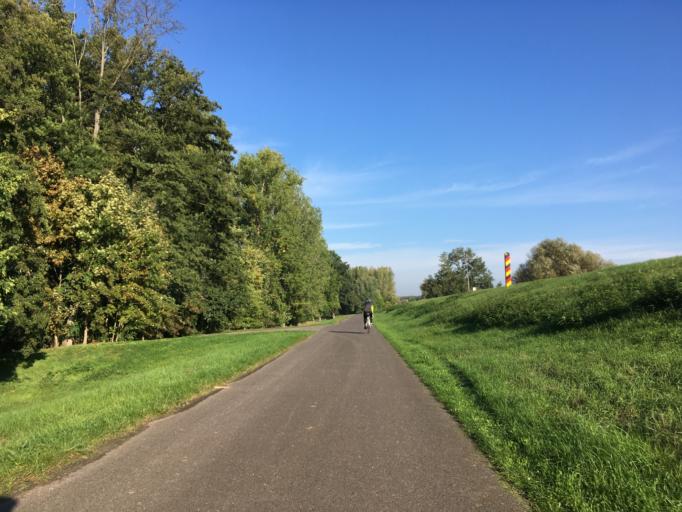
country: DE
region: Brandenburg
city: Reitwein
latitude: 52.5239
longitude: 14.6033
